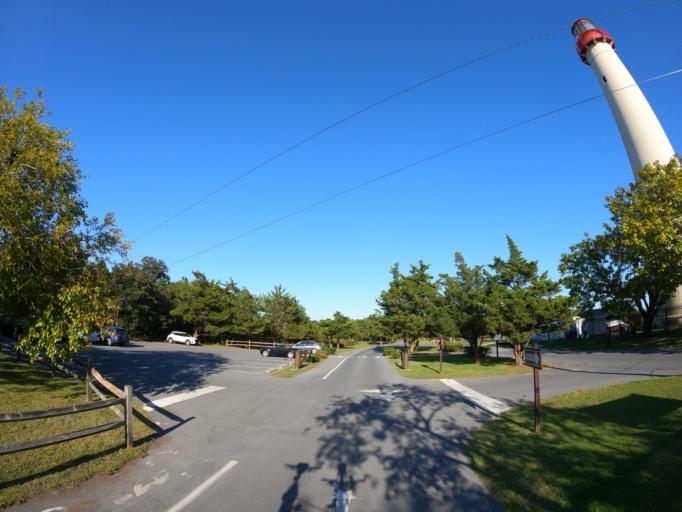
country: US
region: New Jersey
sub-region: Cape May County
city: West Cape May
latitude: 38.9332
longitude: -74.9609
